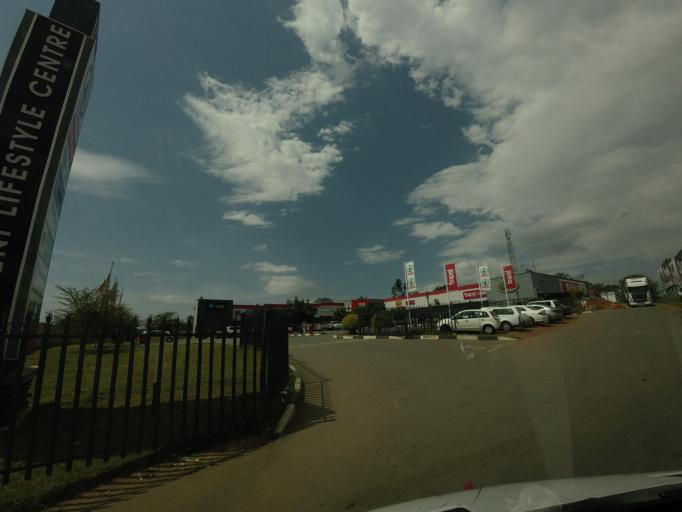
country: SZ
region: Manzini
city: Manzini
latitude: -26.4940
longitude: 31.4017
